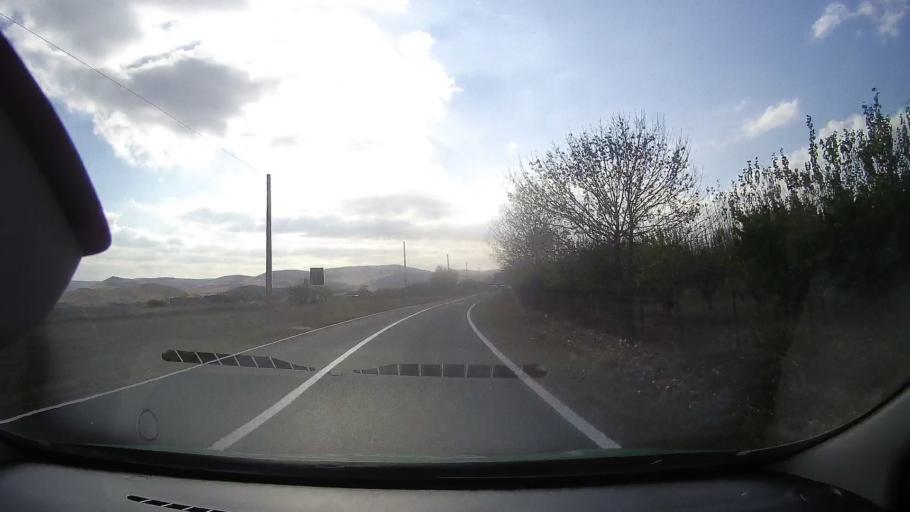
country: RO
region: Tulcea
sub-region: Comuna Nalbant
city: Nicolae Balcescu
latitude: 45.0027
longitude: 28.5965
